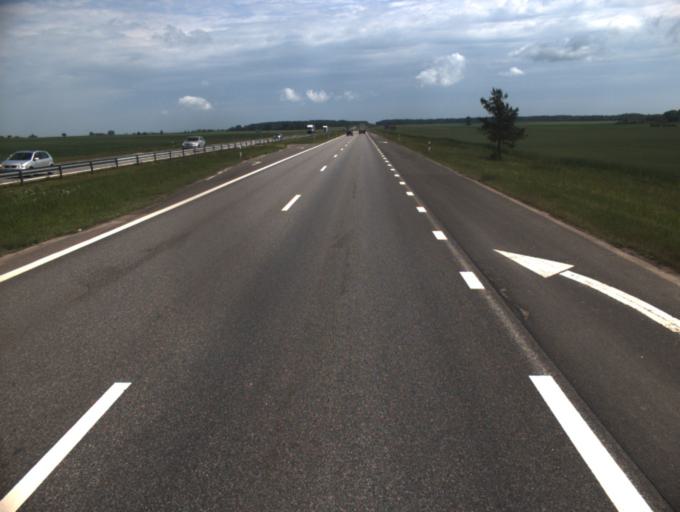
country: LT
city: Ariogala
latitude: 55.2748
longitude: 23.3703
